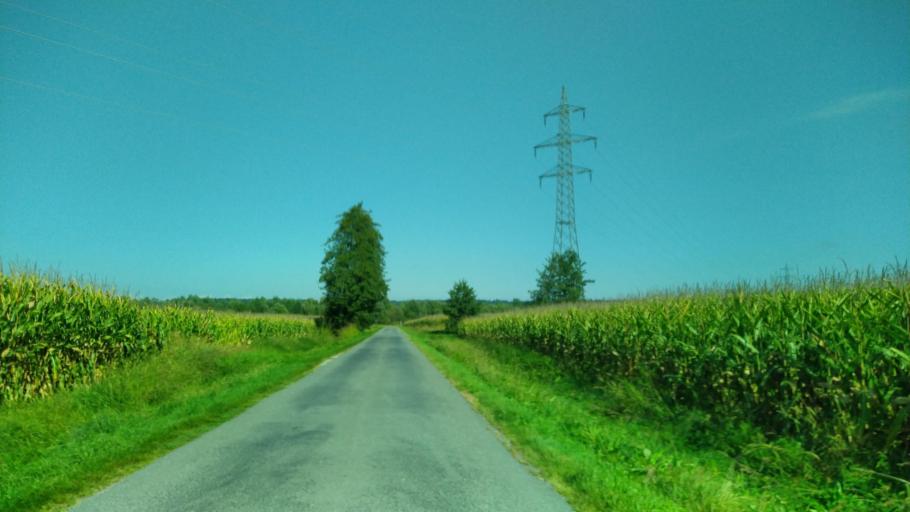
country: AT
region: Styria
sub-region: Politischer Bezirk Deutschlandsberg
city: Wettmannstatten
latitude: 46.8249
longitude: 15.3556
